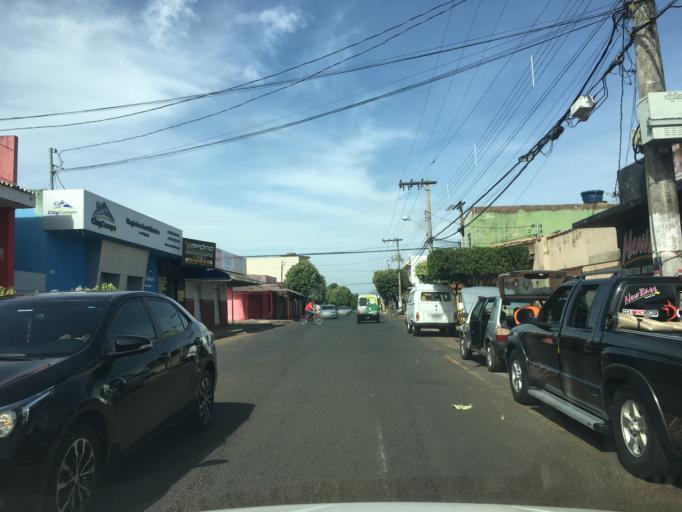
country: BR
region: Minas Gerais
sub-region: Uberlandia
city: Uberlandia
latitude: -18.9417
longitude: -48.3125
